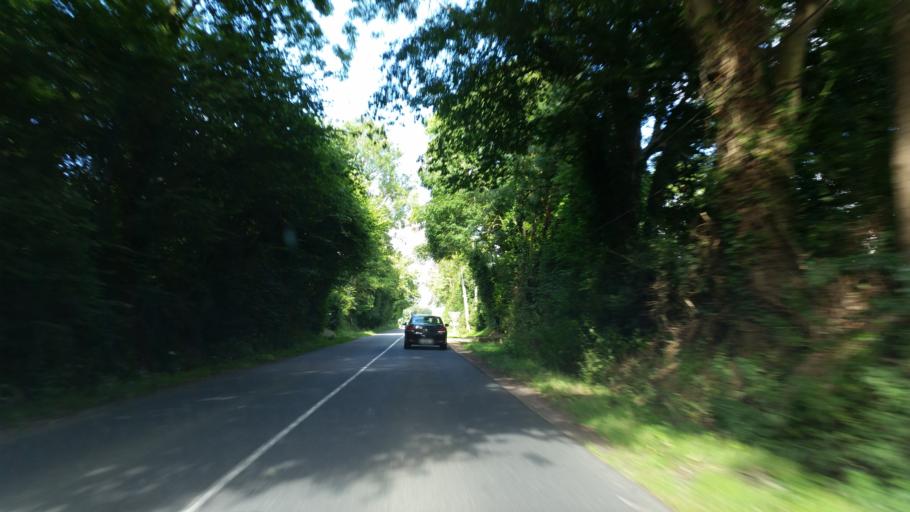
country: FR
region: Lower Normandy
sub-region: Departement du Calvados
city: Dozule
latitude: 49.2688
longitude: -0.0344
